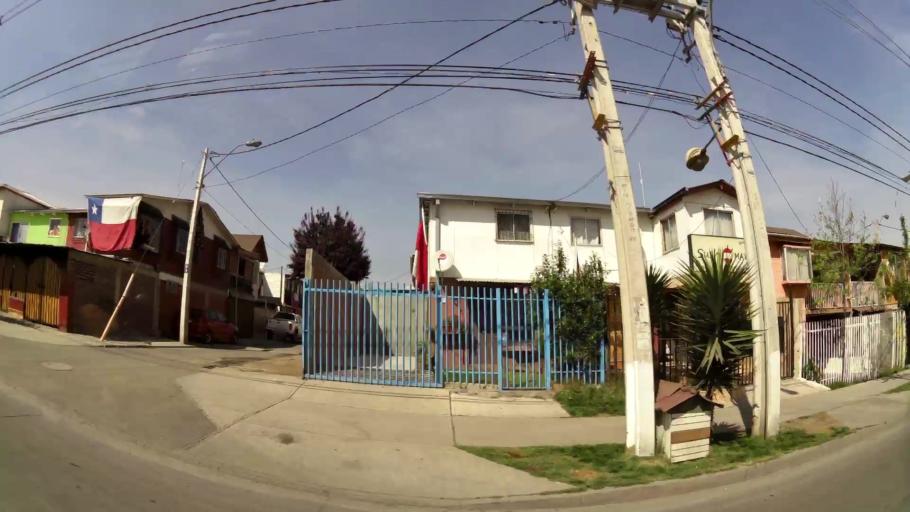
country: CL
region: Santiago Metropolitan
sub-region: Provincia de Santiago
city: Villa Presidente Frei, Nunoa, Santiago, Chile
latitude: -33.5115
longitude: -70.5623
